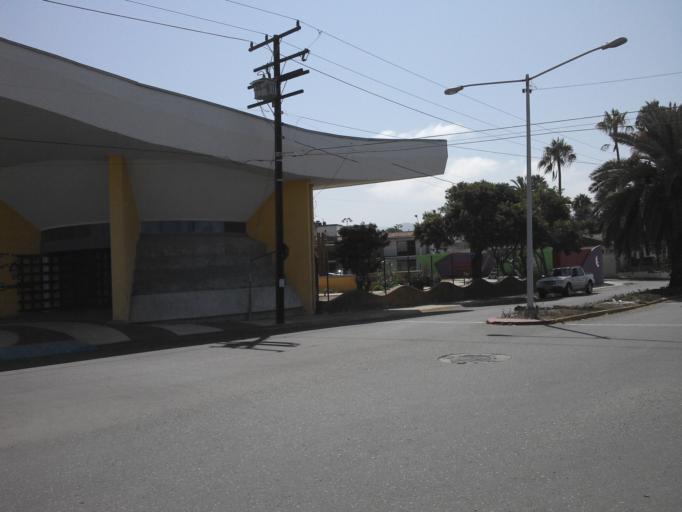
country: MX
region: Baja California
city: Ensenada
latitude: 31.8580
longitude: -116.6162
